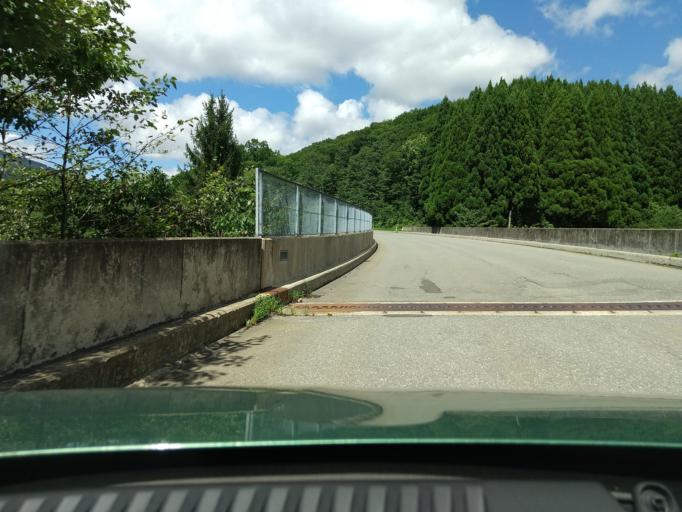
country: JP
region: Iwate
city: Shizukuishi
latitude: 39.7736
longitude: 140.7638
